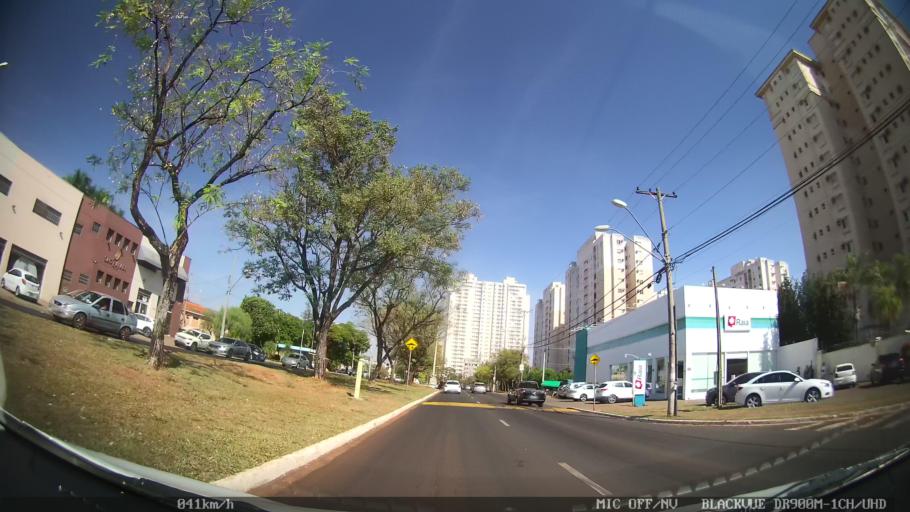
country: BR
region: Sao Paulo
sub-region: Ribeirao Preto
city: Ribeirao Preto
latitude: -21.1968
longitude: -47.8227
